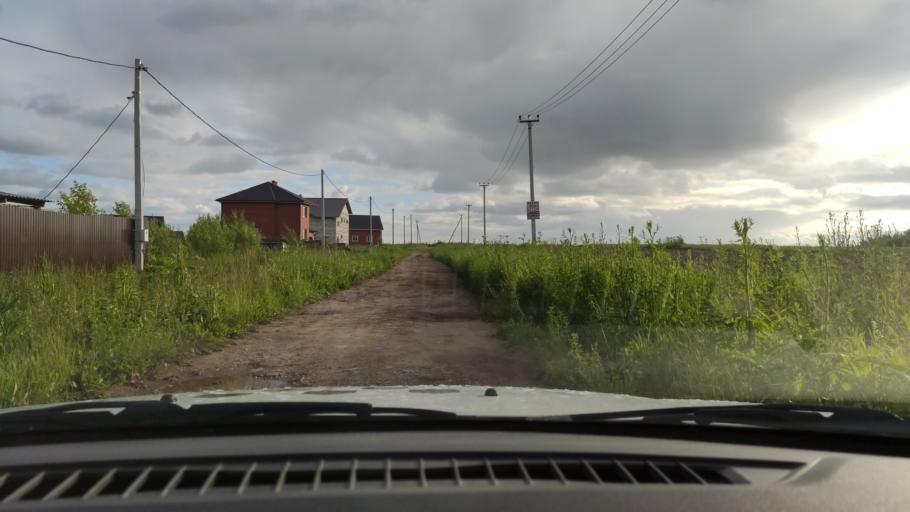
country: RU
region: Perm
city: Perm
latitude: 58.0350
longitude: 56.3797
